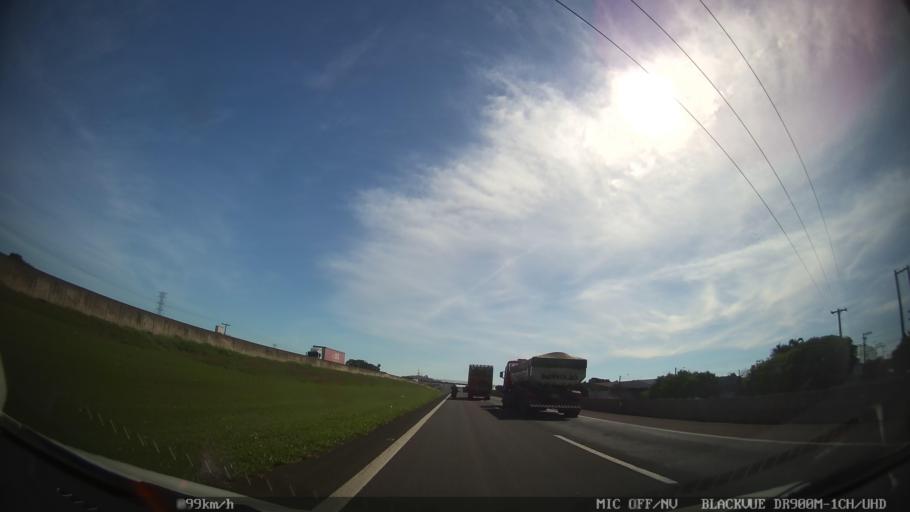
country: BR
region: Sao Paulo
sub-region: Leme
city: Leme
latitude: -22.1838
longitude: -47.3983
